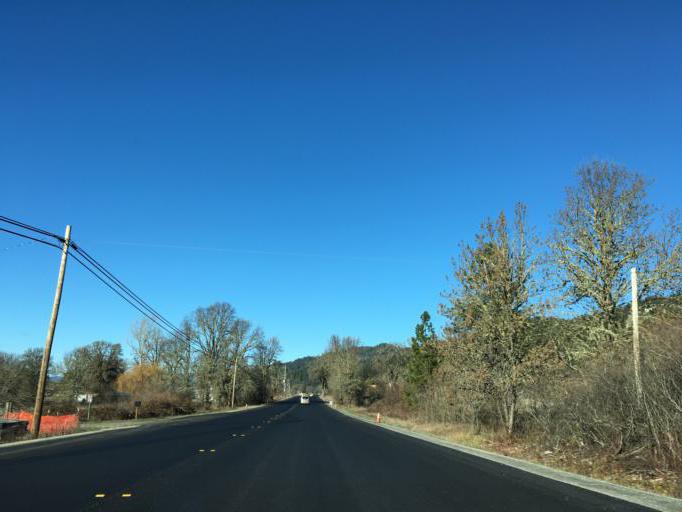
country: US
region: California
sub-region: Mendocino County
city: Laytonville
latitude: 39.6630
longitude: -123.4762
